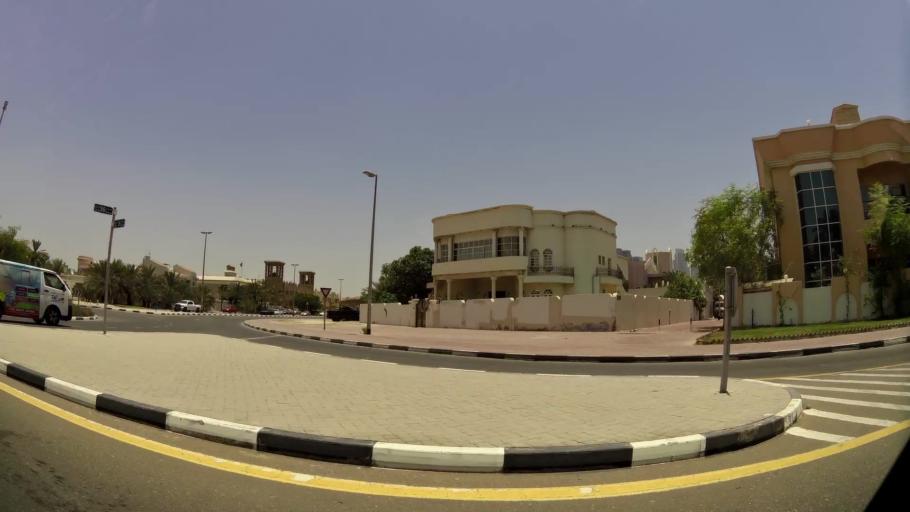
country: AE
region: Ash Shariqah
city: Sharjah
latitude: 25.2426
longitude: 55.2864
